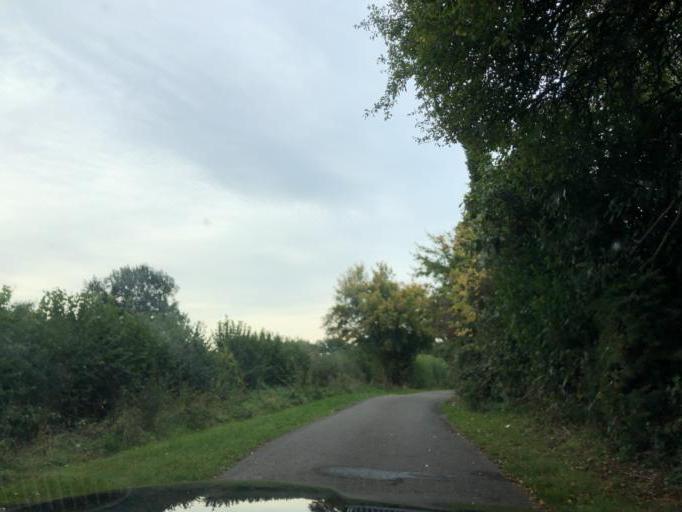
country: GB
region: England
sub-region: Warwickshire
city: Wroxall
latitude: 52.3229
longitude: -1.6546
